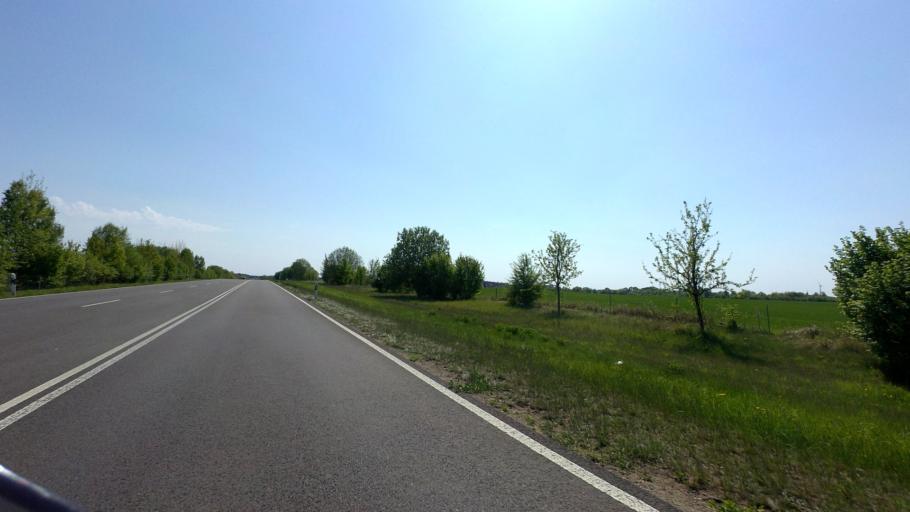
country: DE
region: Brandenburg
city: Beeskow
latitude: 52.1777
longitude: 14.2167
